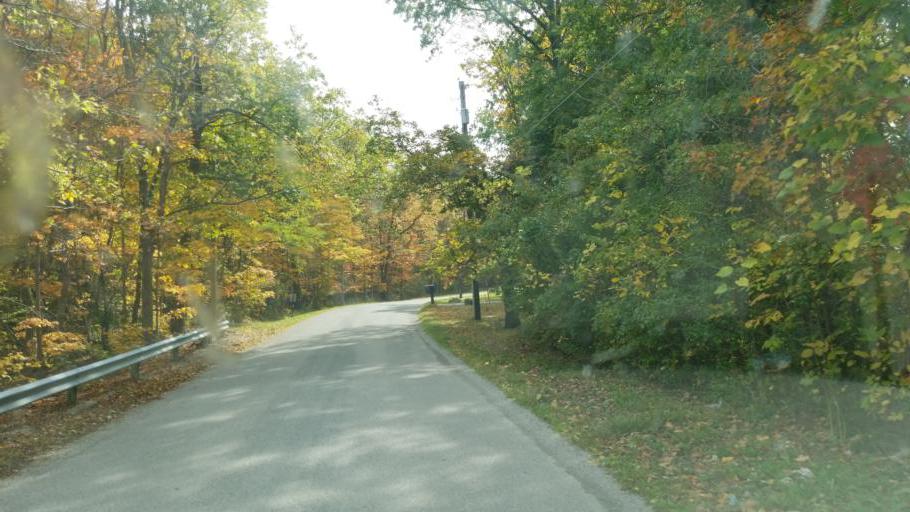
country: US
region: Ohio
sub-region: Lorain County
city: Vermilion-on-the-Lake
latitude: 41.3886
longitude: -82.3304
